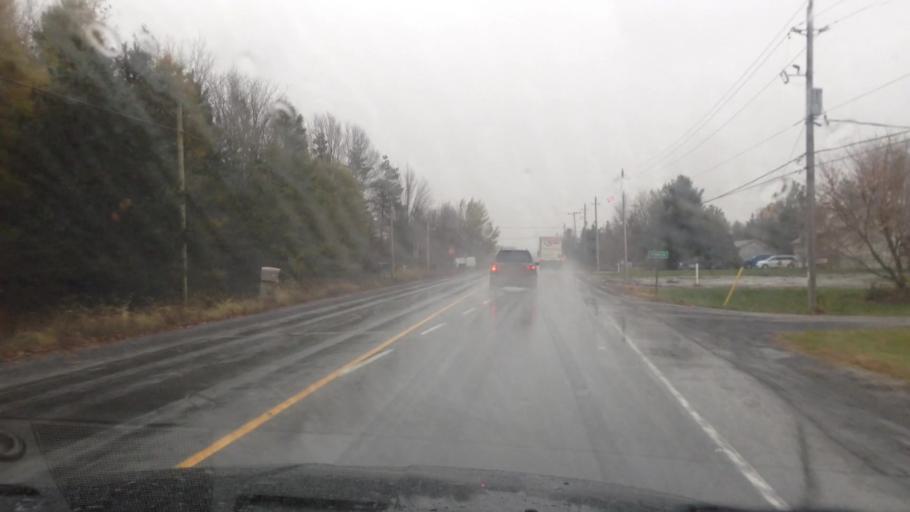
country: CA
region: Ontario
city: Bourget
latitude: 45.2756
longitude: -75.3141
